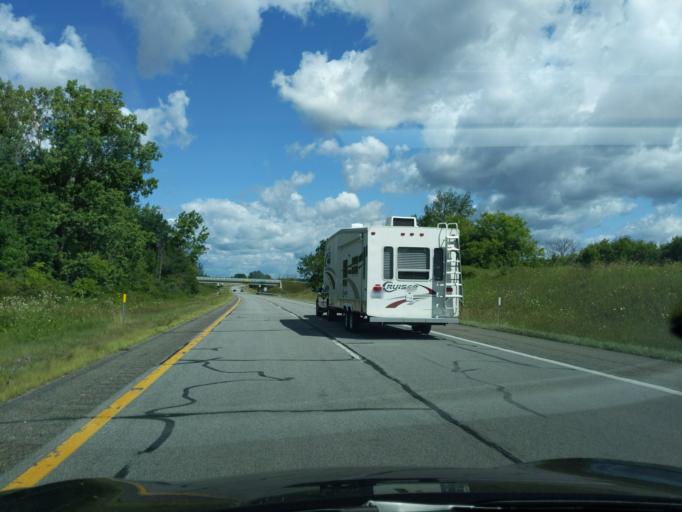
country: US
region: Michigan
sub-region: Clare County
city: Clare
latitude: 43.7546
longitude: -84.7572
